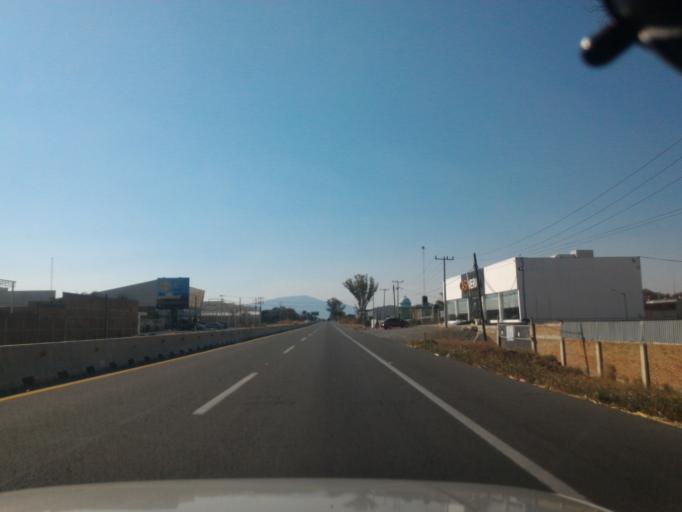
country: MX
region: Jalisco
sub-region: Poncitlan
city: Santa Cruz el Grande
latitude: 20.3656
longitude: -102.8544
